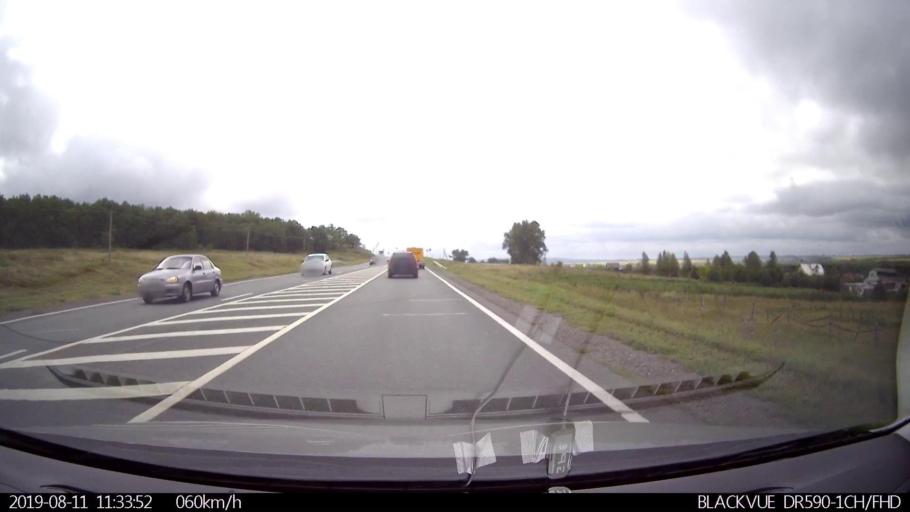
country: RU
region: Ulyanovsk
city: Silikatnyy
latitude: 54.0234
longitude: 48.2144
